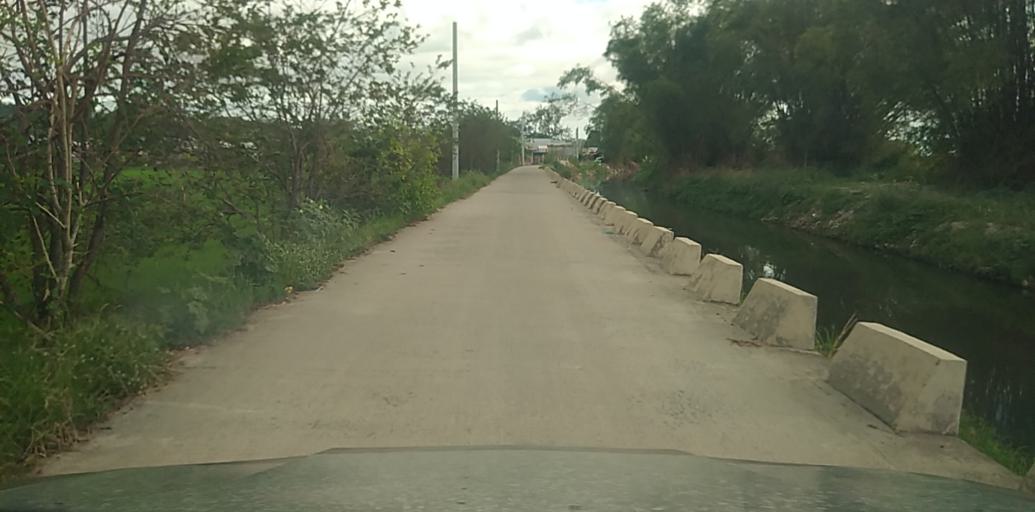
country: PH
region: Central Luzon
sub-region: Province of Pampanga
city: Panlinlang
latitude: 15.1777
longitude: 120.7021
